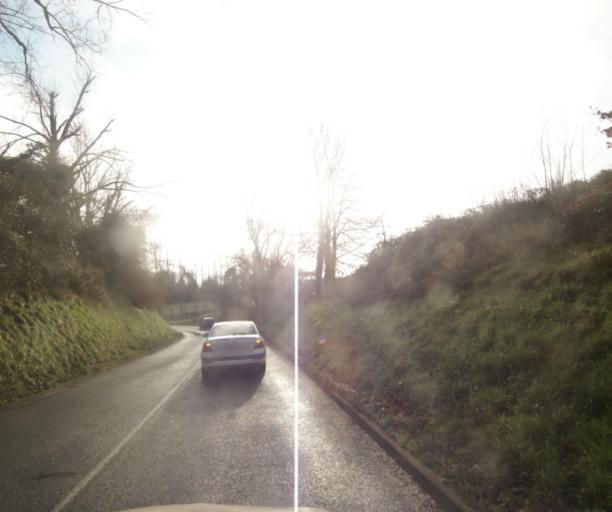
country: FR
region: Nord-Pas-de-Calais
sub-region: Departement du Nord
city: Artres
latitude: 50.2933
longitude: 3.5334
